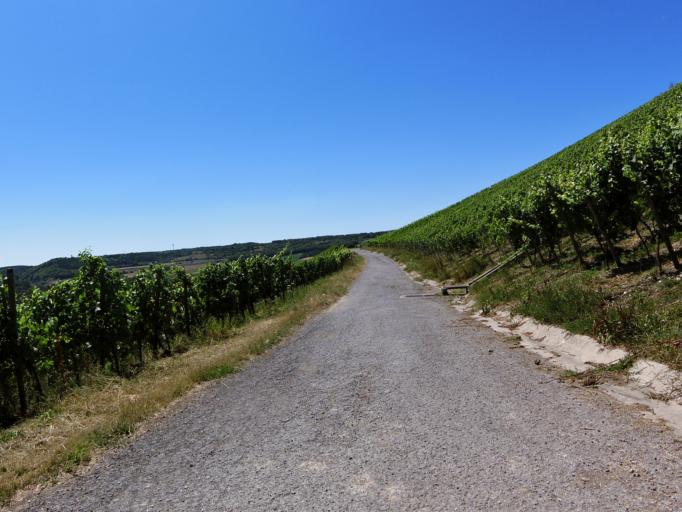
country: DE
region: Bavaria
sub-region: Regierungsbezirk Unterfranken
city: Randersacker
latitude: 49.7565
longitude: 9.9883
